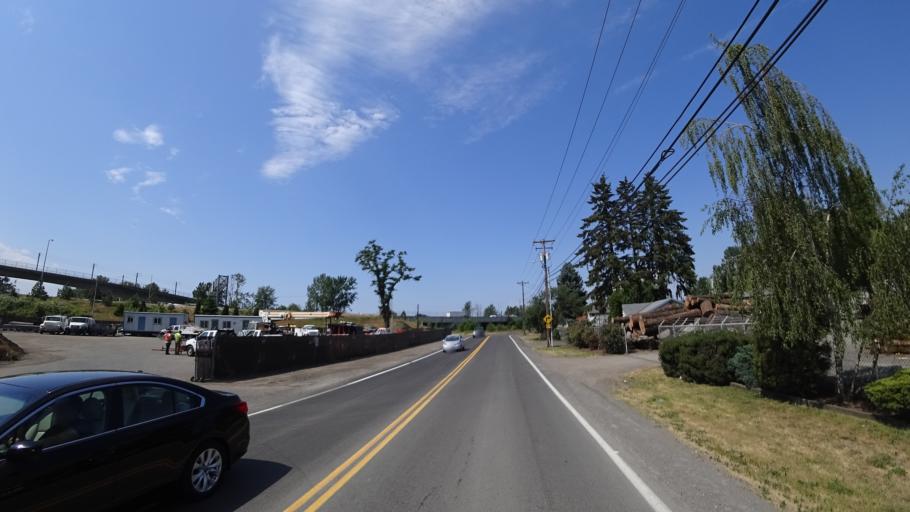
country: US
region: Oregon
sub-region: Multnomah County
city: Lents
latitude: 45.5654
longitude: -122.5547
